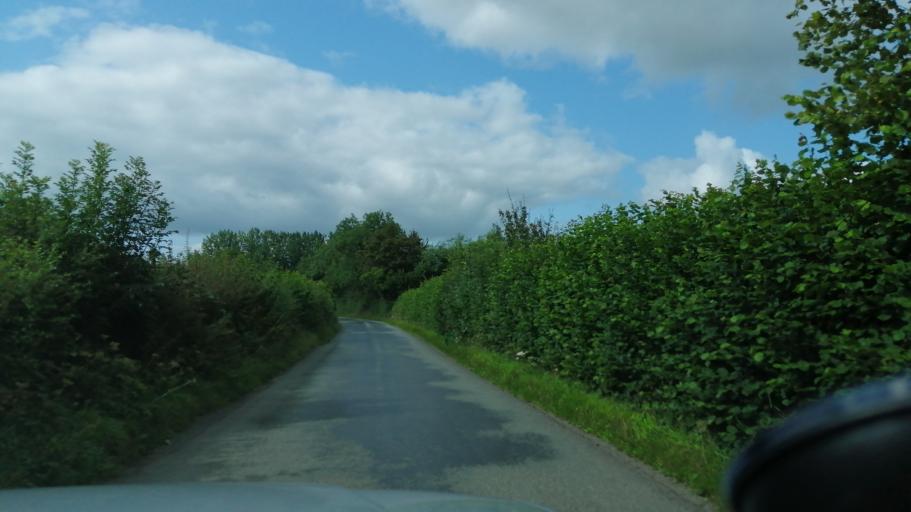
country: GB
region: England
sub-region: Herefordshire
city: Kinnersley
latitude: 52.1242
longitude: -2.9619
